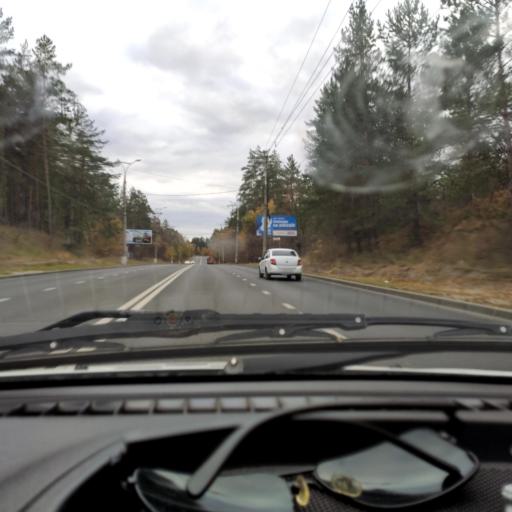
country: RU
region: Samara
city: Zhigulevsk
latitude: 53.4937
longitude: 49.4629
